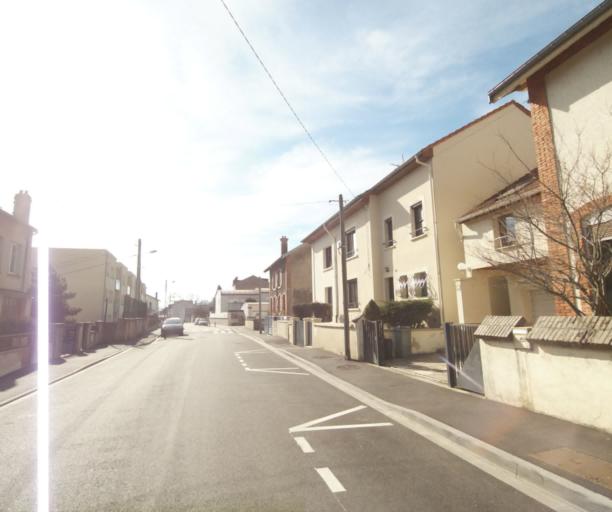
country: FR
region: Lorraine
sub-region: Departement de Meurthe-et-Moselle
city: Maxeville
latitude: 48.7161
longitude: 6.1674
